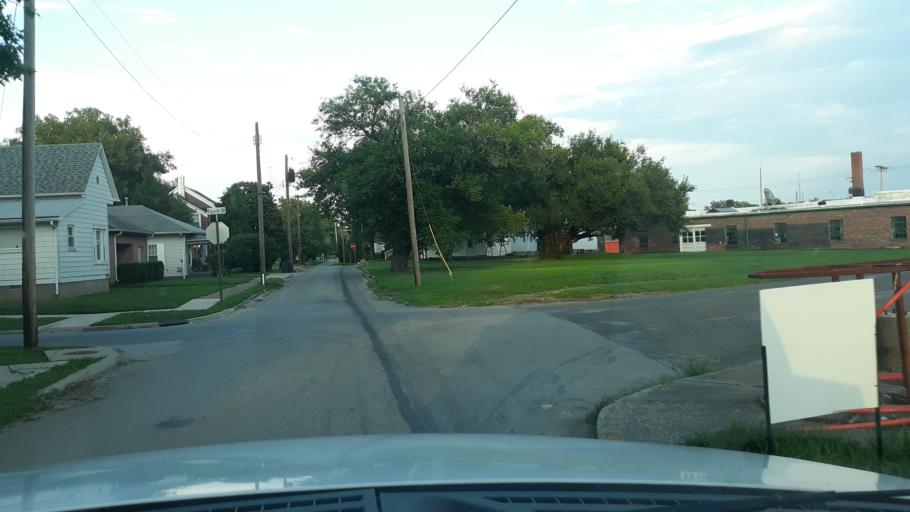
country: US
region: Illinois
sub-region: Saline County
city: Eldorado
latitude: 37.8152
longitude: -88.4398
